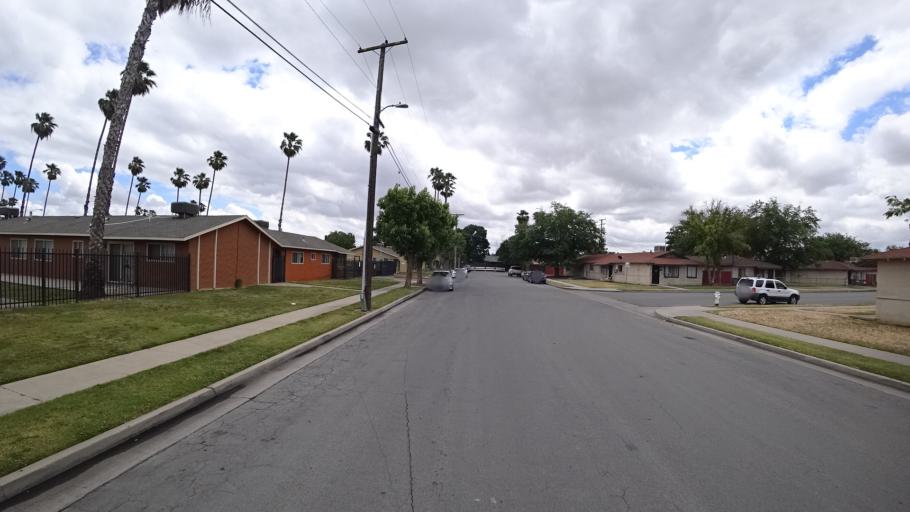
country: US
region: California
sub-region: Kings County
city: Hanford
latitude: 36.3376
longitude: -119.6264
